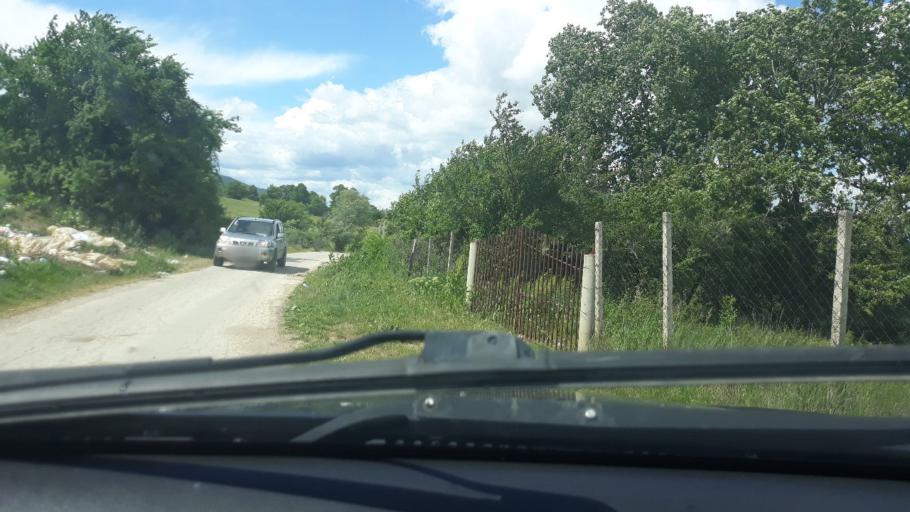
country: MK
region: Krivogastani
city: Krivogashtani
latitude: 41.3245
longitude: 21.3039
